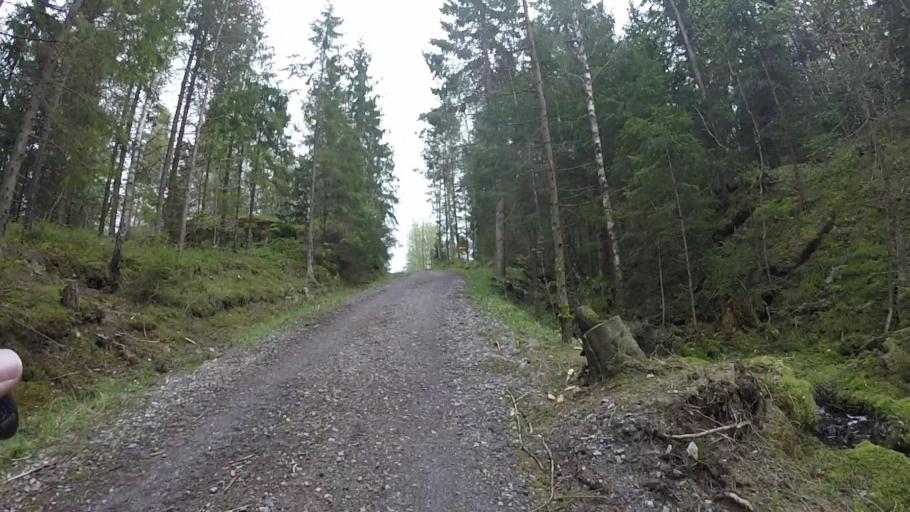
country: SE
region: Vaestra Goetaland
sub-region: Trollhattan
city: Sjuntorp
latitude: 58.2395
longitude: 12.2081
